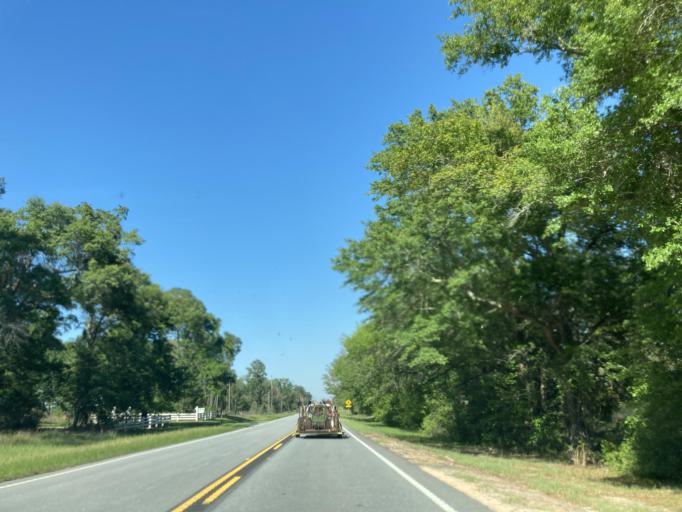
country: US
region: Georgia
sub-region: Baker County
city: Newton
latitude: 31.4445
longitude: -84.2669
